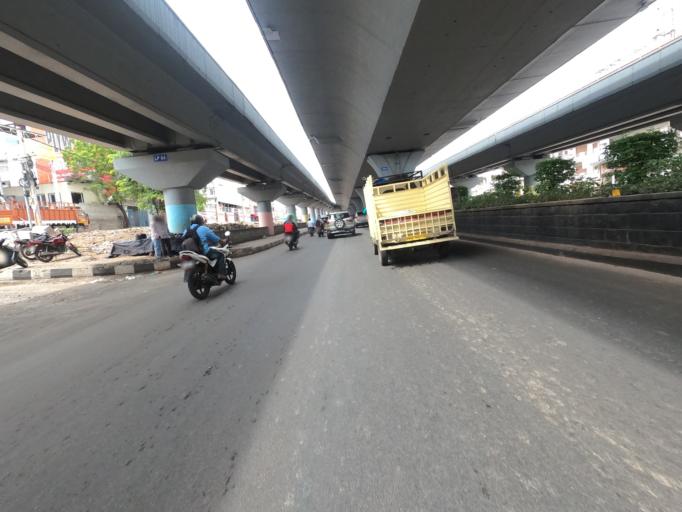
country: IN
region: Telangana
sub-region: Hyderabad
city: Hyderabad
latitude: 17.3492
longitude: 78.4169
